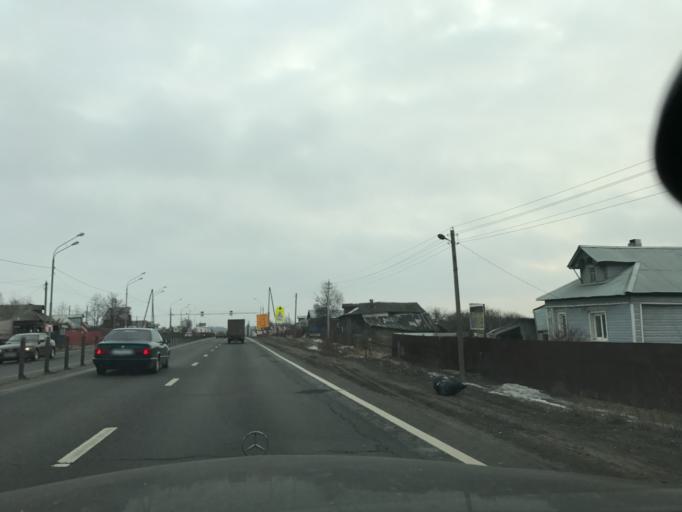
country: RU
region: Moskovskaya
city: Demikhovo
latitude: 55.8549
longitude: 38.8735
